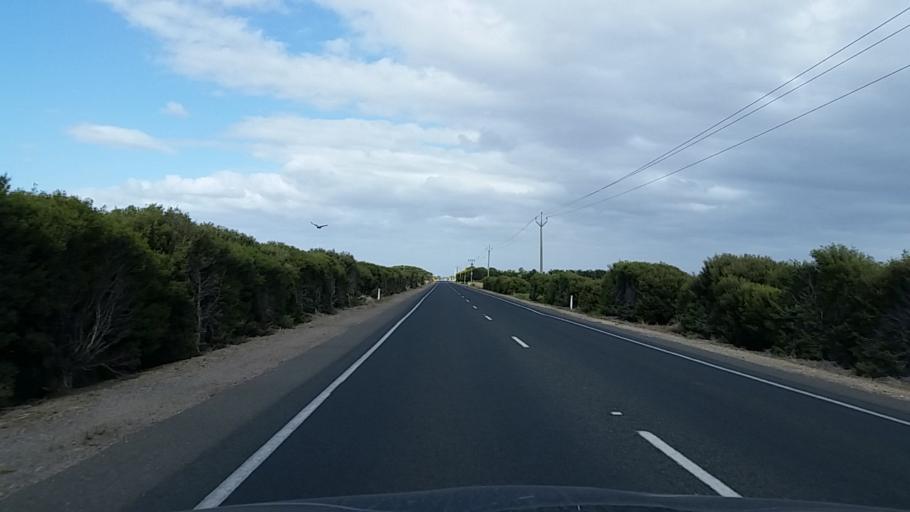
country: AU
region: South Australia
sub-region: Alexandrina
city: Port Elliot
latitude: -35.5090
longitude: 138.7289
